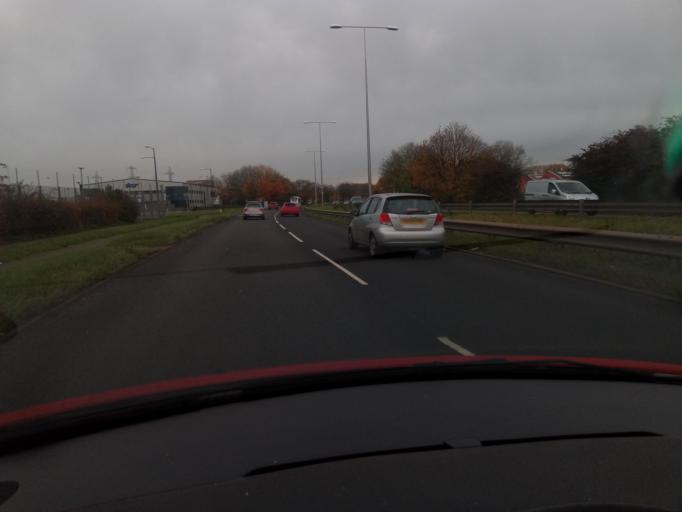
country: GB
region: England
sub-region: Derbyshire
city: Borrowash
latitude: 52.9082
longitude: -1.4308
